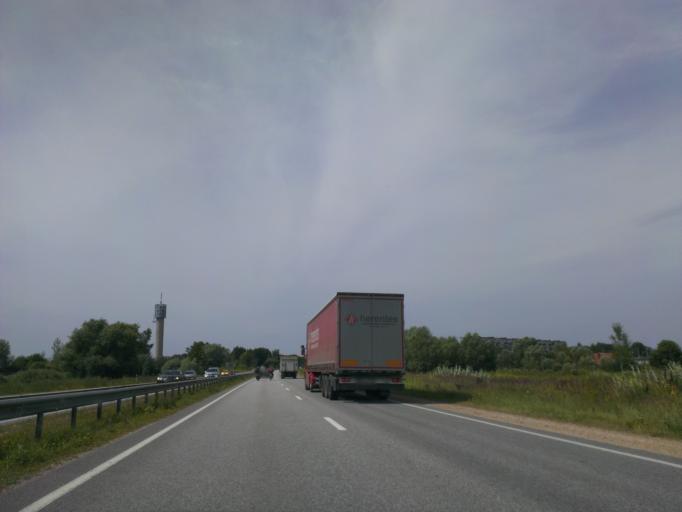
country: LV
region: Salaspils
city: Salaspils
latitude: 56.8485
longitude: 24.3484
